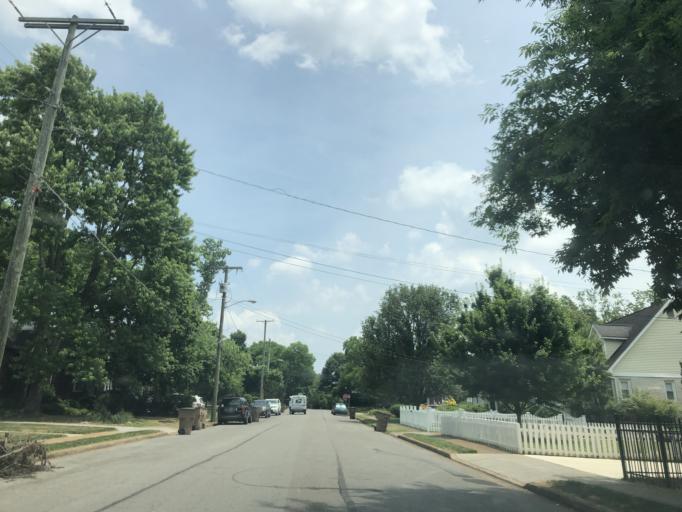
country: US
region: Tennessee
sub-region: Davidson County
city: Nashville
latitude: 36.1291
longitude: -86.8085
